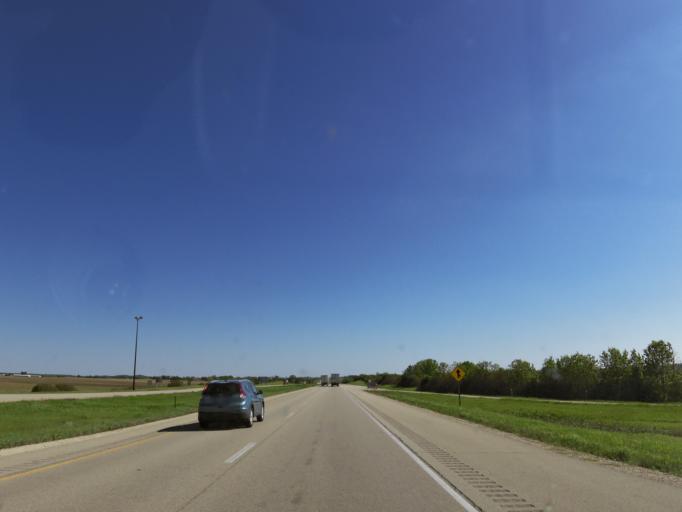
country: US
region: Illinois
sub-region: Ogle County
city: Rochelle
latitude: 41.7584
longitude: -89.0099
